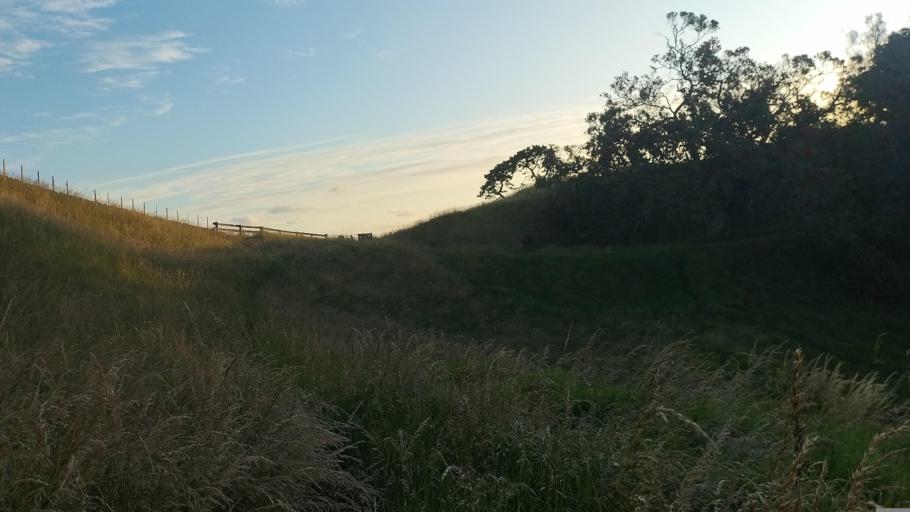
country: NZ
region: Auckland
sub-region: Auckland
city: Auckland
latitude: -36.9003
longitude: 174.7826
